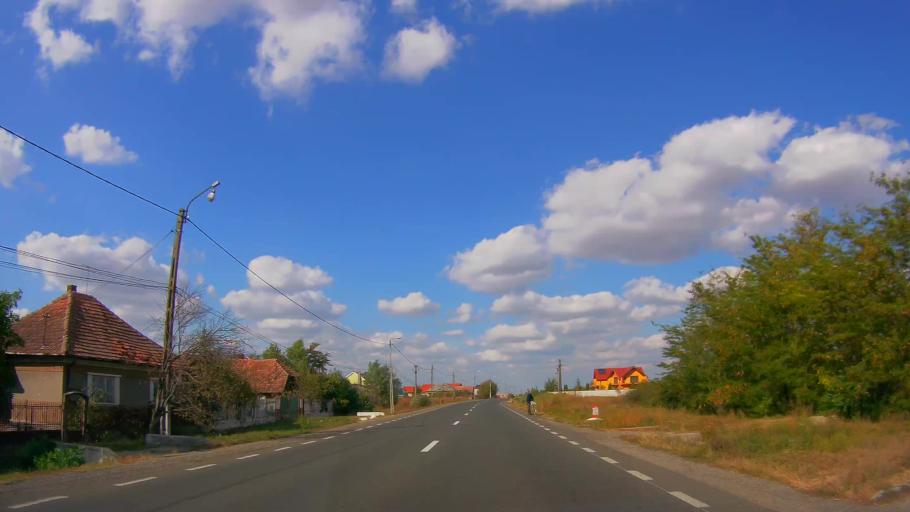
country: RO
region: Satu Mare
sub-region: Oras Ardud
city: Madaras
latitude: 47.6888
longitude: 22.8650
